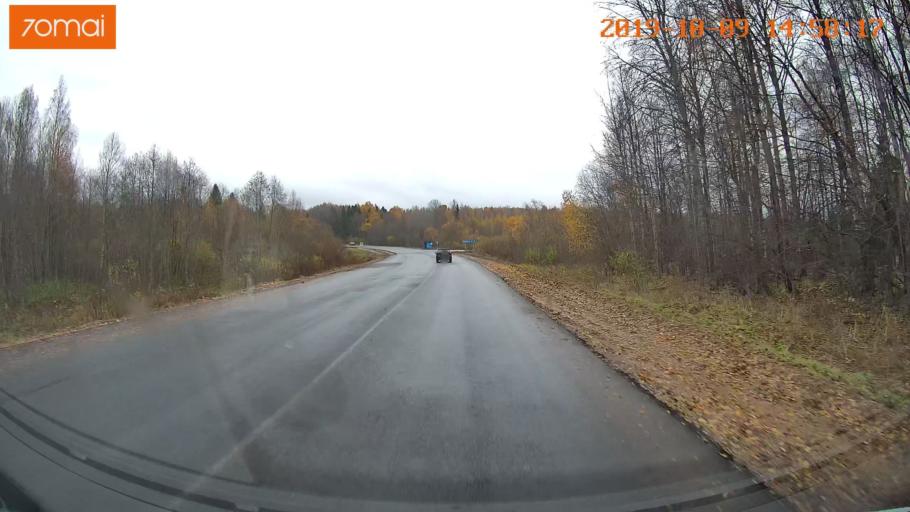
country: RU
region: Kostroma
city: Chistyye Bory
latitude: 58.3284
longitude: 41.6541
